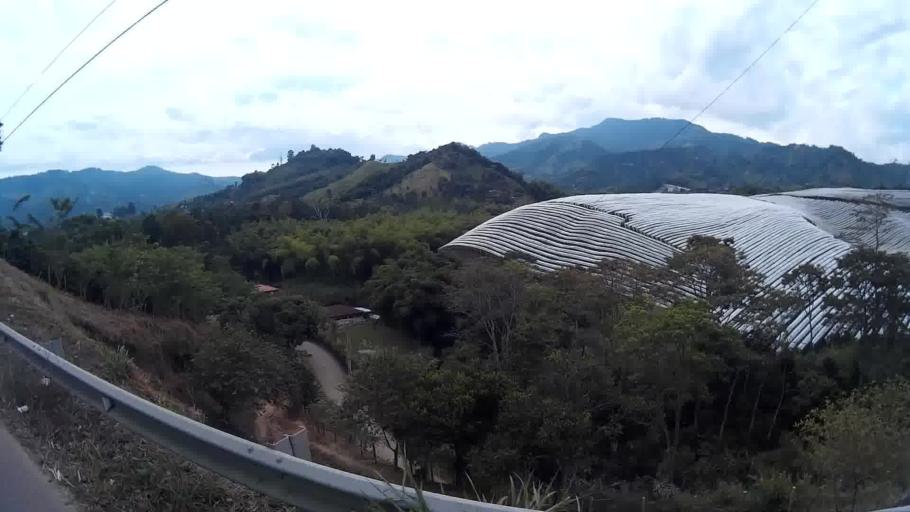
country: CO
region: Risaralda
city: Pereira
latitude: 4.8393
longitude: -75.7567
